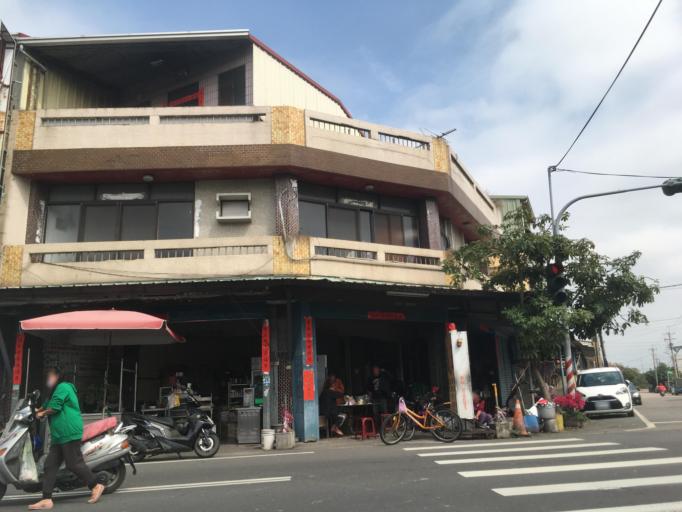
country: TW
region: Taiwan
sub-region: Yunlin
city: Douliu
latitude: 23.6915
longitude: 120.4676
